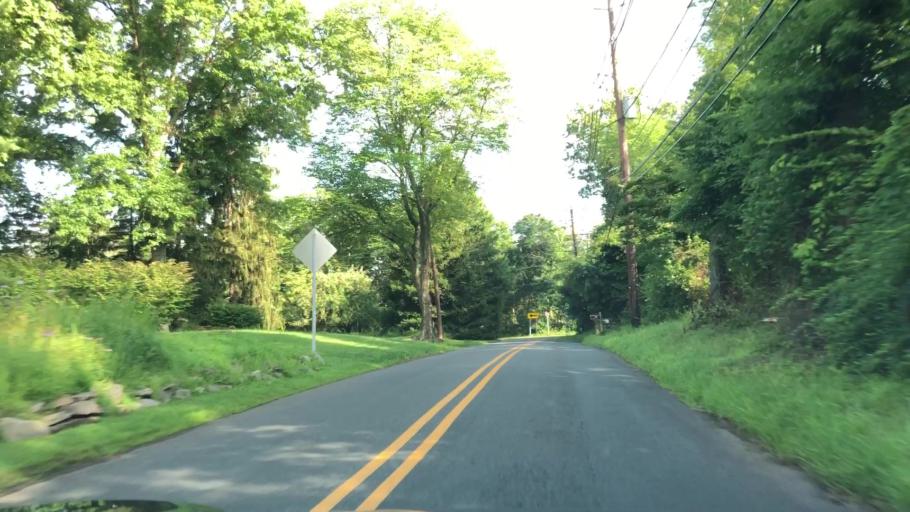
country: US
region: New Jersey
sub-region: Mercer County
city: Pennington
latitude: 40.3510
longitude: -74.7757
